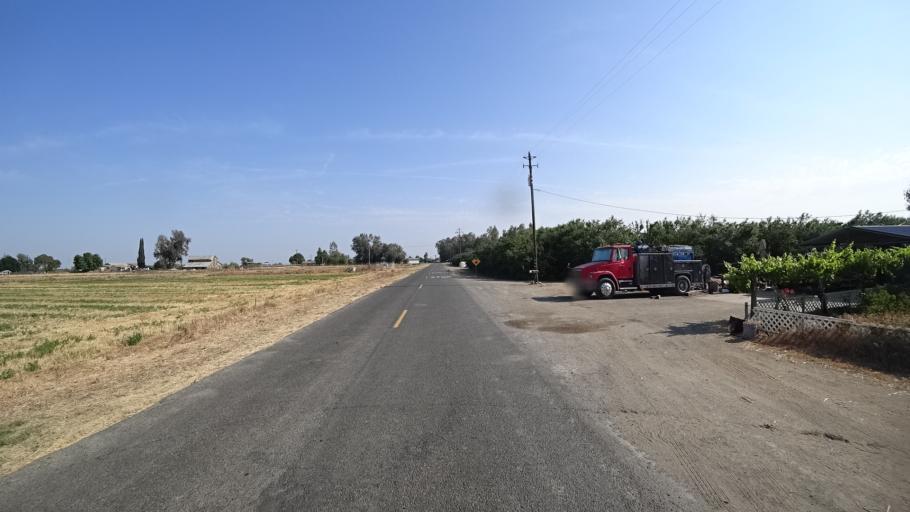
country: US
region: California
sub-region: Fresno County
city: Riverdale
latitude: 36.3783
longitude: -119.8161
